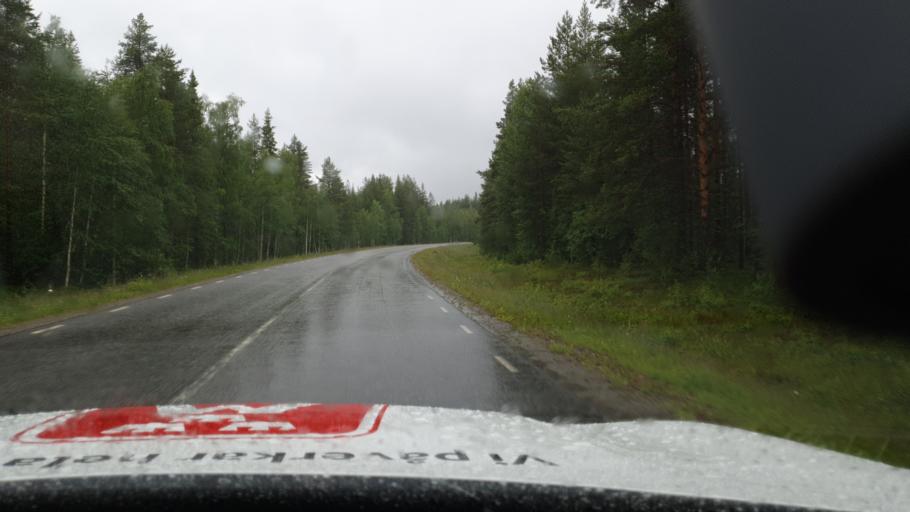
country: SE
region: Vaesterbotten
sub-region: Skelleftea Kommun
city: Langsele
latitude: 64.7956
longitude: 20.0172
